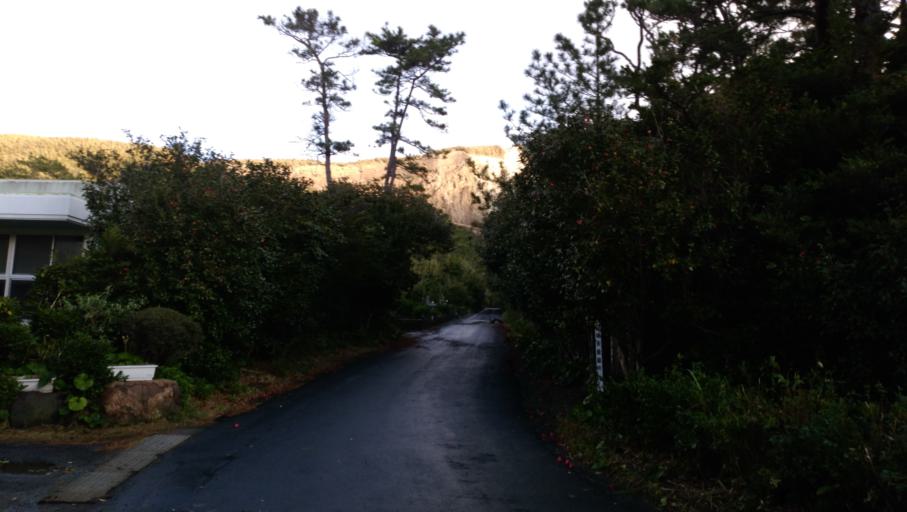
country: JP
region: Kagoshima
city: Makurazaki
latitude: 30.7839
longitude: 130.2796
